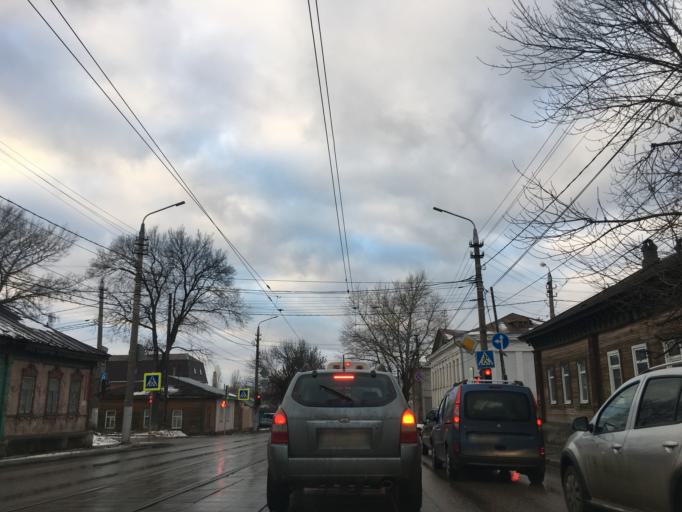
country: RU
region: Tula
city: Tula
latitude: 54.1996
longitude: 37.6340
